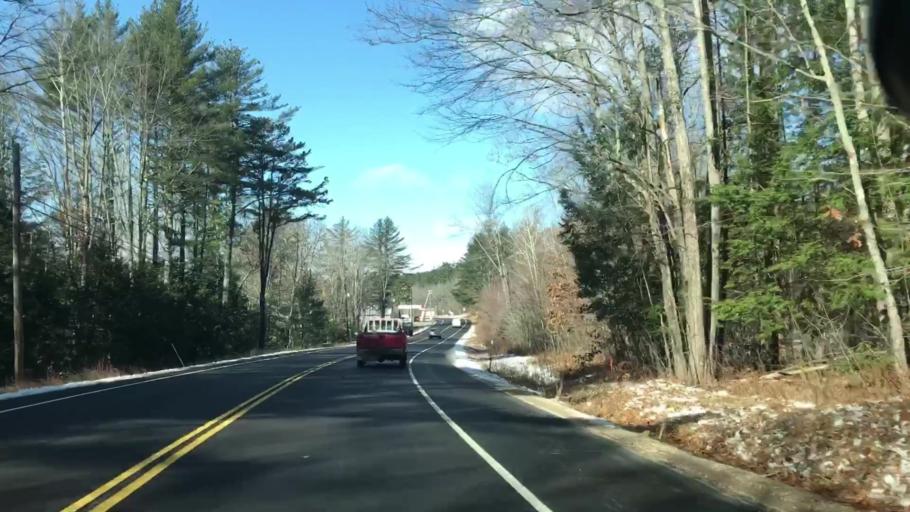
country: US
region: New Hampshire
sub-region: Carroll County
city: Effingham
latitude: 43.7944
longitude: -70.9960
